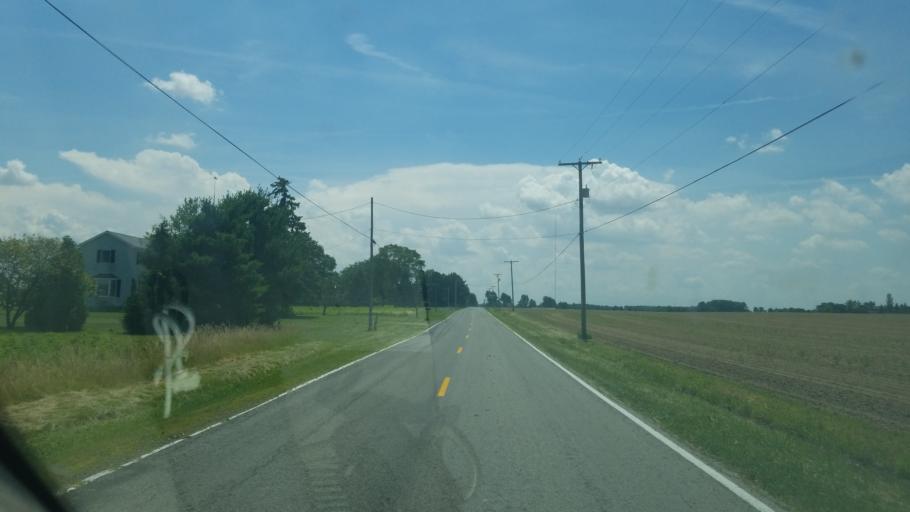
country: US
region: Ohio
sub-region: Hancock County
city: Arlington
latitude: 40.9262
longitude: -83.5946
